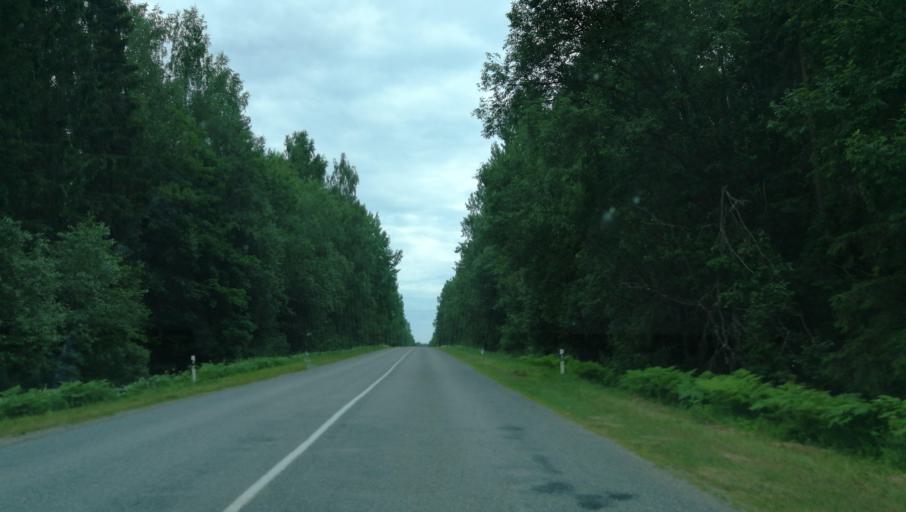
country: LV
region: Valmieras Rajons
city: Valmiera
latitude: 57.6992
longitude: 25.4278
